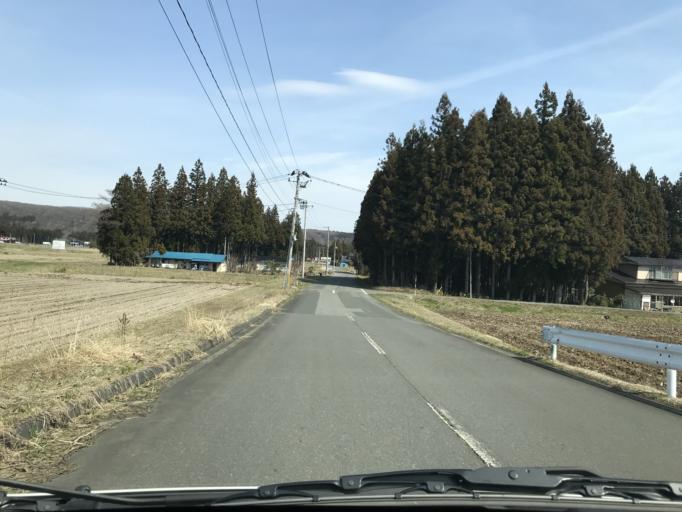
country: JP
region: Iwate
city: Mizusawa
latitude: 39.1193
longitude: 141.0133
